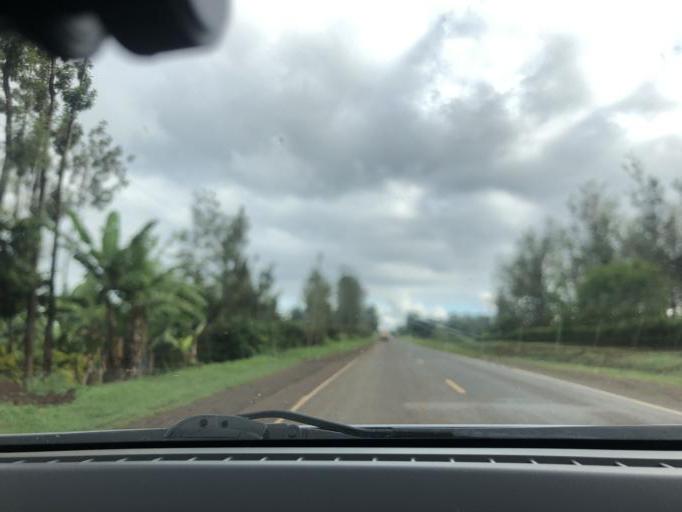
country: KE
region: Murang'a District
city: Maragua
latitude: -0.8193
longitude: 37.1399
